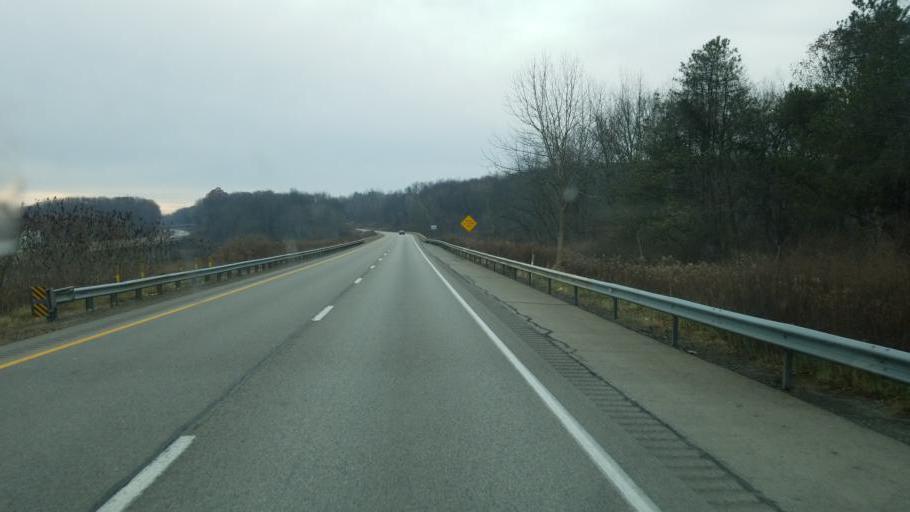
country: US
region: Pennsylvania
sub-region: Mercer County
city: Stoneboro
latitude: 41.4309
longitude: -80.1648
